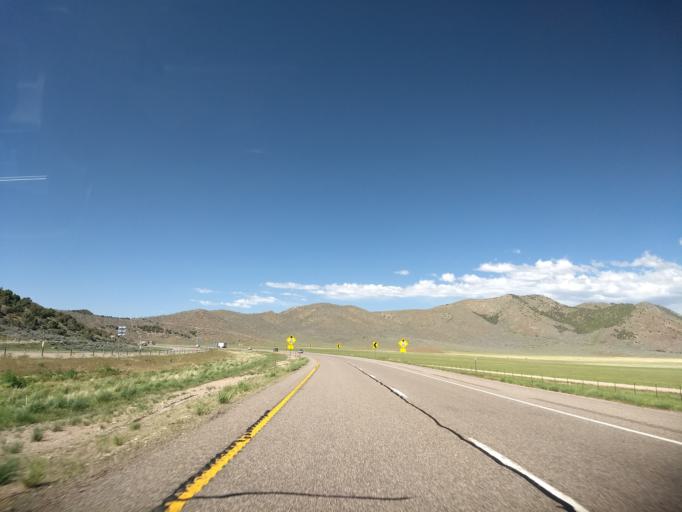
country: US
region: Utah
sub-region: Beaver County
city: Beaver
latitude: 38.6654
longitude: -112.5896
